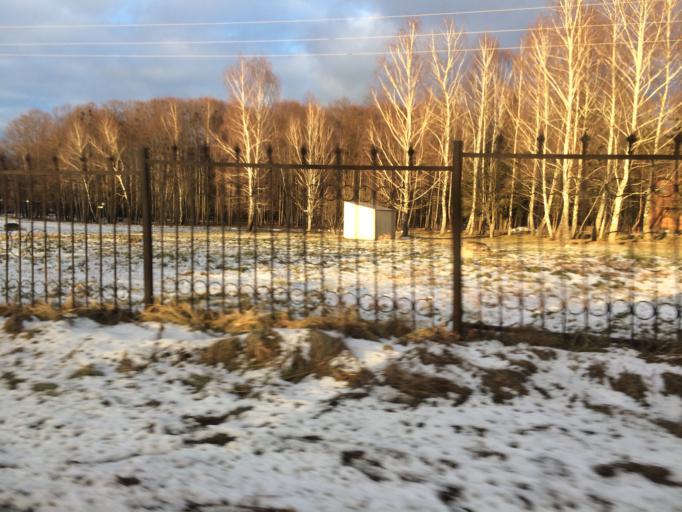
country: RU
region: Tula
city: Cherepet'
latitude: 54.1118
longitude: 36.3361
